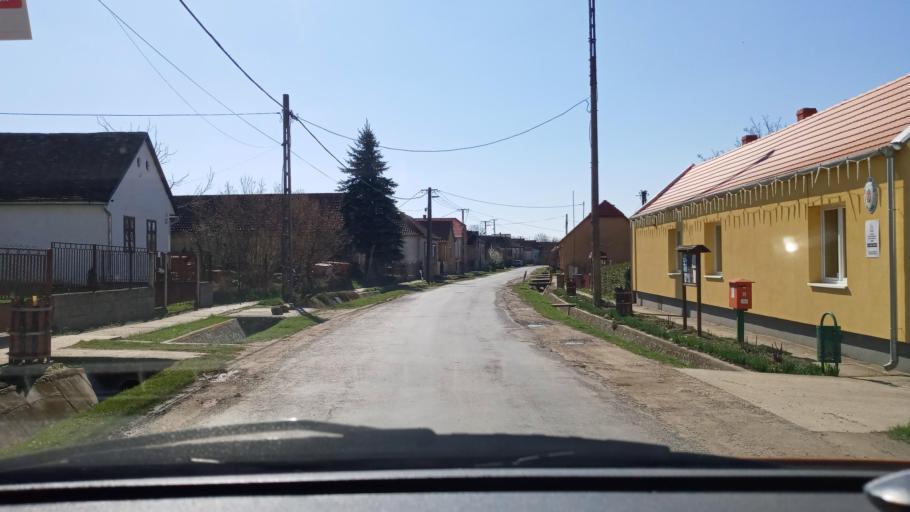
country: HU
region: Baranya
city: Kozarmisleny
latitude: 46.0585
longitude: 18.3762
